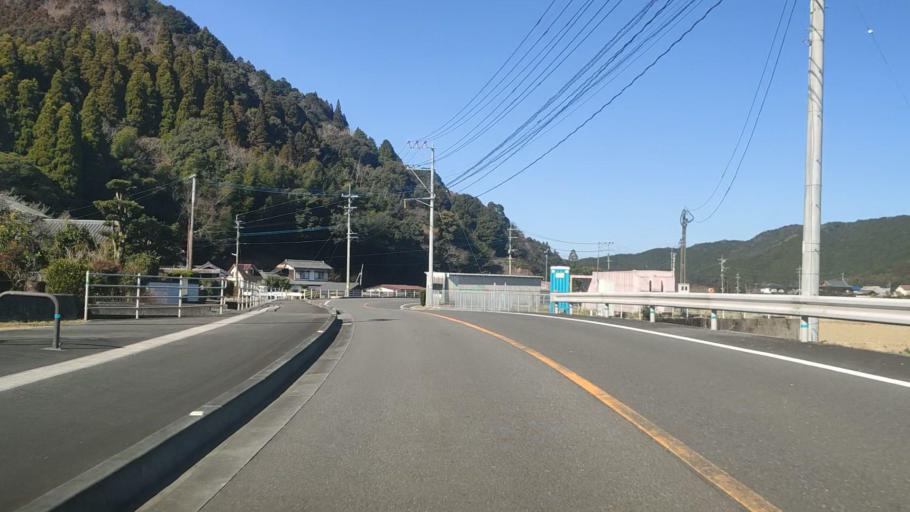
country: JP
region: Oita
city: Saiki
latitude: 32.9277
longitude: 131.9225
